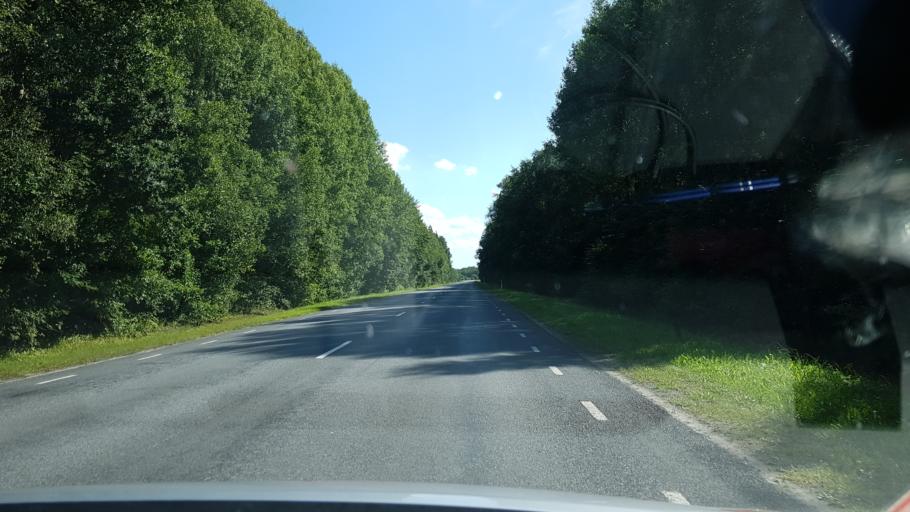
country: EE
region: Laeaene
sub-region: Lihula vald
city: Lihula
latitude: 58.8195
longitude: 23.7746
